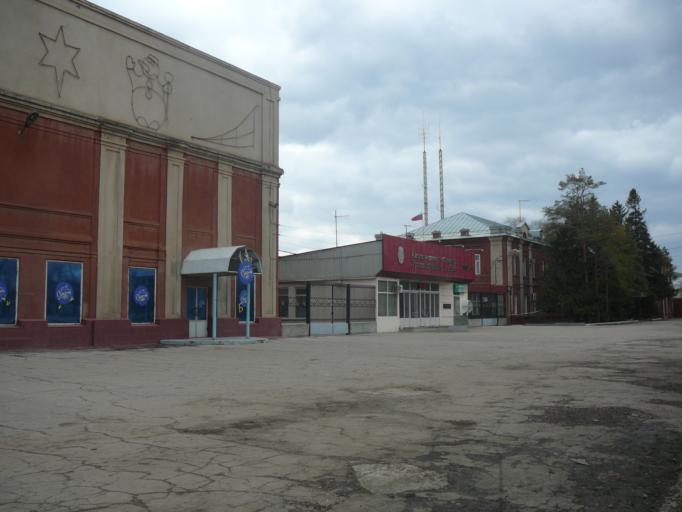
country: RU
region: Saratov
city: Engel's
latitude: 51.4653
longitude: 46.1184
